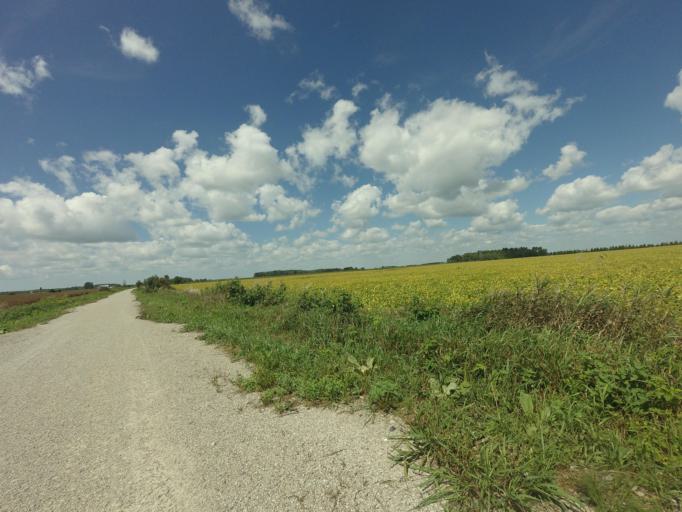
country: CA
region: Ontario
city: North Perth
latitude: 43.5631
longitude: -81.0151
